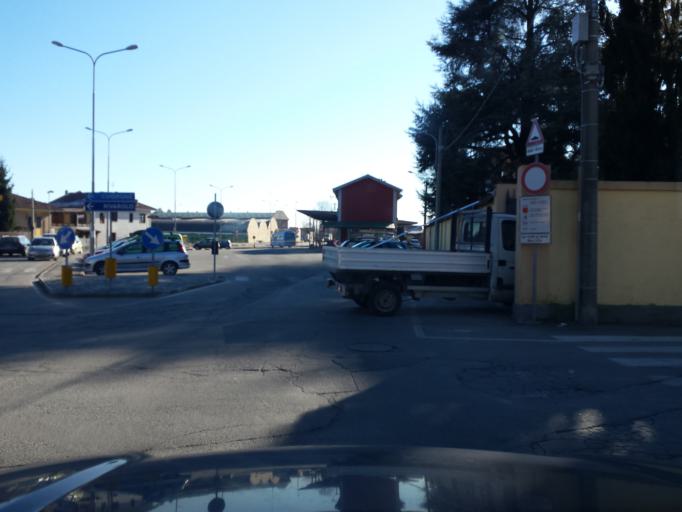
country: IT
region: Piedmont
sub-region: Provincia di Torino
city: Castellamonte
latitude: 45.3818
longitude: 7.7156
